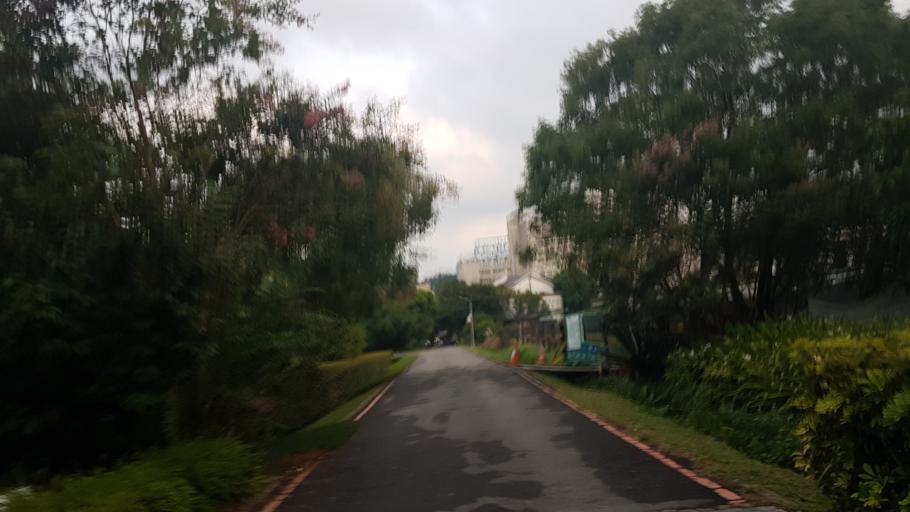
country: TW
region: Taipei
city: Taipei
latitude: 25.0165
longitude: 121.5403
